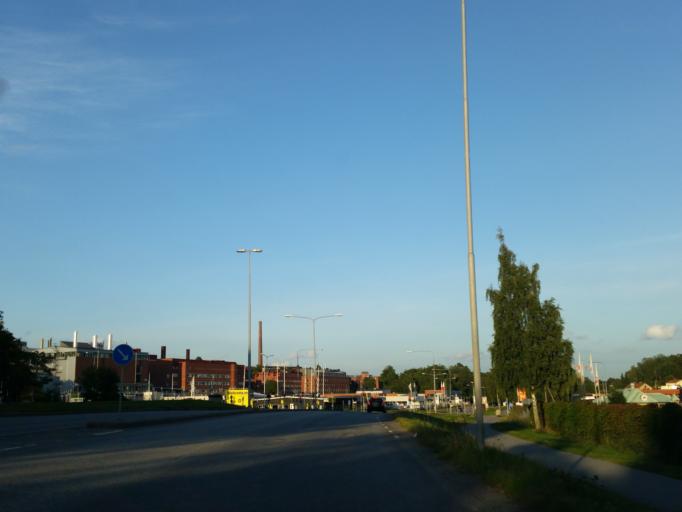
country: SE
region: Stockholm
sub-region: Sodertalje Kommun
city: Soedertaelje
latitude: 59.2029
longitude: 17.6062
